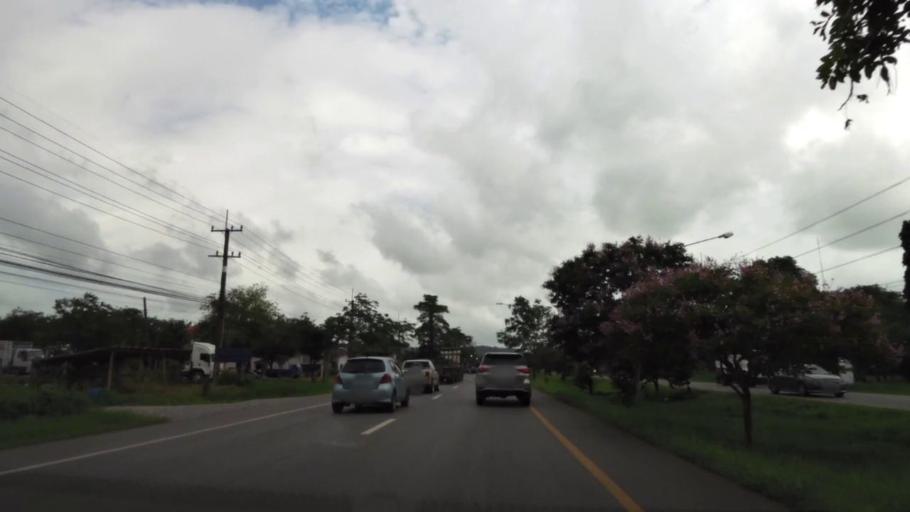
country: TH
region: Chanthaburi
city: Na Yai Am
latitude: 12.7325
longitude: 101.9073
